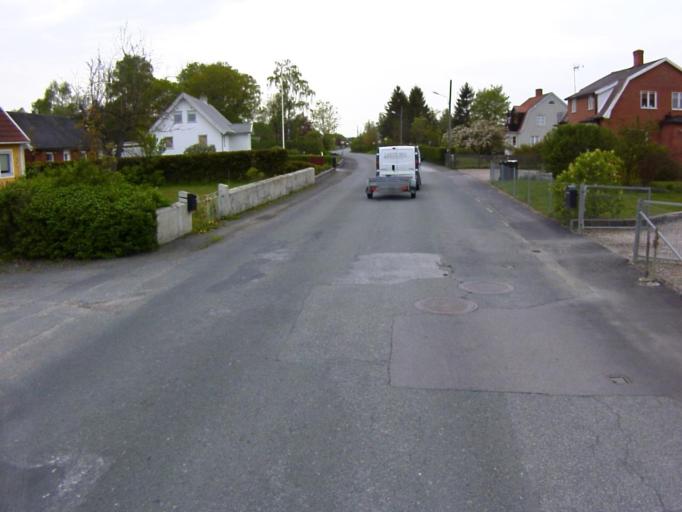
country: SE
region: Skane
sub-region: Kristianstads Kommun
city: Onnestad
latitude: 55.9319
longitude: 14.0047
